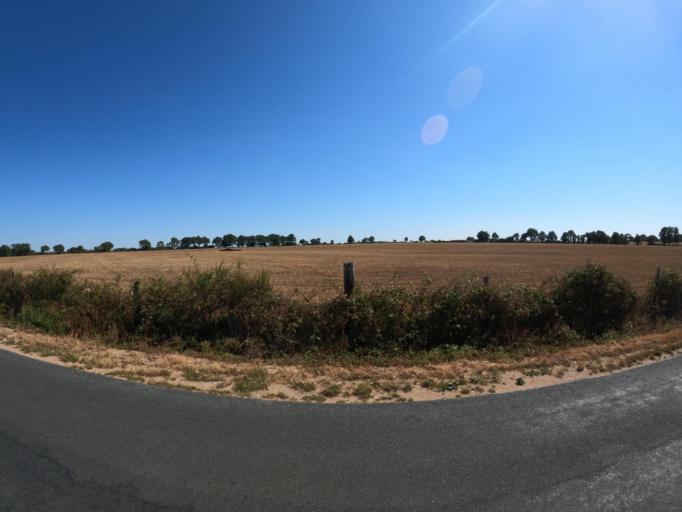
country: FR
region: Pays de la Loire
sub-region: Departement de la Vendee
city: La Boissiere-de-Montaigu
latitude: 46.9600
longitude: -1.1566
